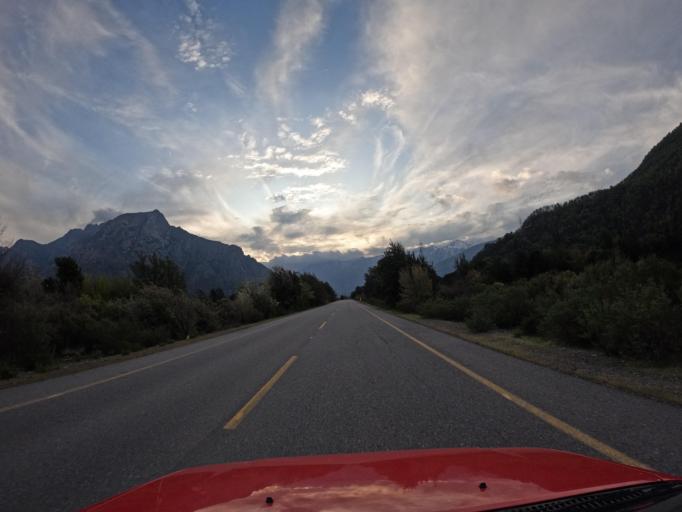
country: CL
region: Maule
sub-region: Provincia de Linares
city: Colbun
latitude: -35.7132
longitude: -71.0545
